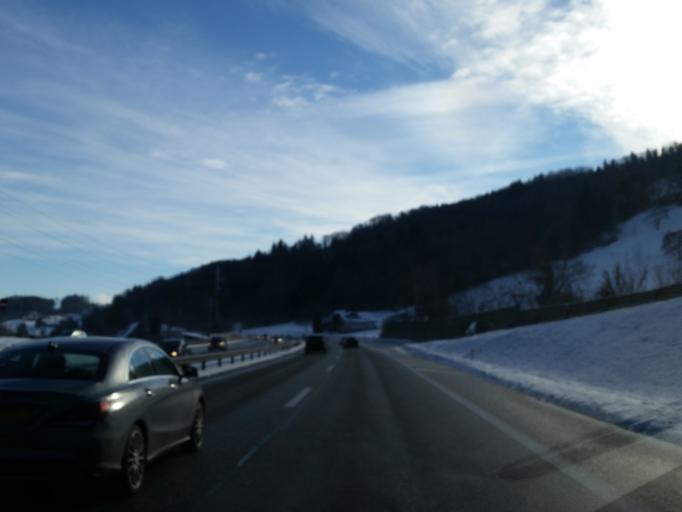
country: CH
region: Schwyz
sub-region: Bezirk Hoefe
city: Freienbach
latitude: 47.1952
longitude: 8.7604
